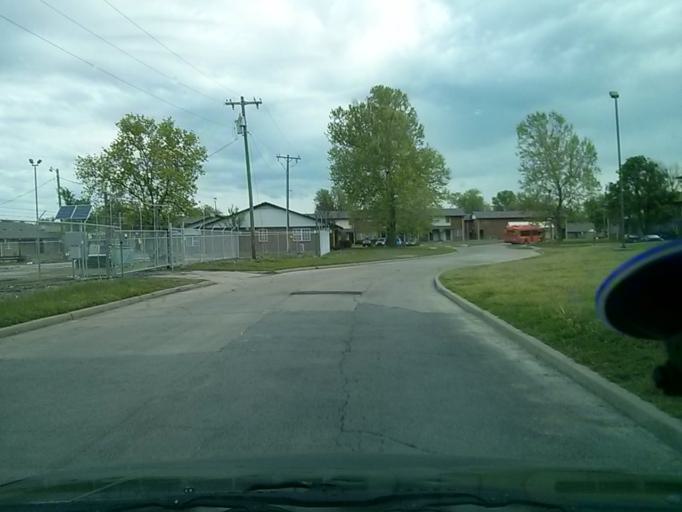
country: US
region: Oklahoma
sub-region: Rogers County
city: Catoosa
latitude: 36.1615
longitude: -95.8406
